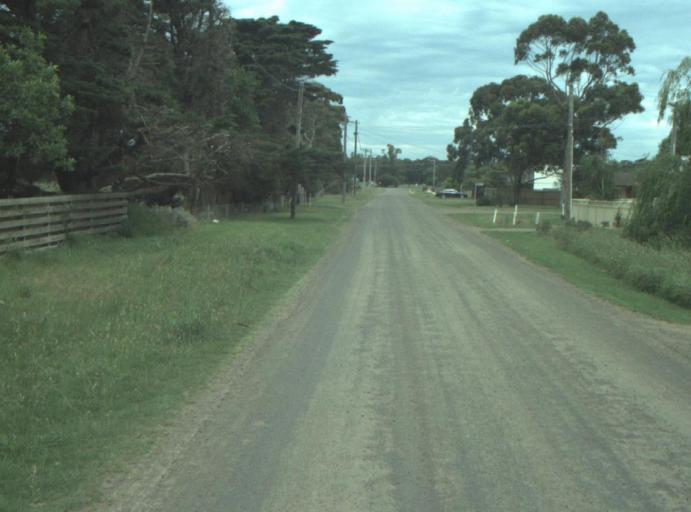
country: AU
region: Victoria
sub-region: Greater Geelong
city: Clifton Springs
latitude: -38.1197
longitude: 144.6692
